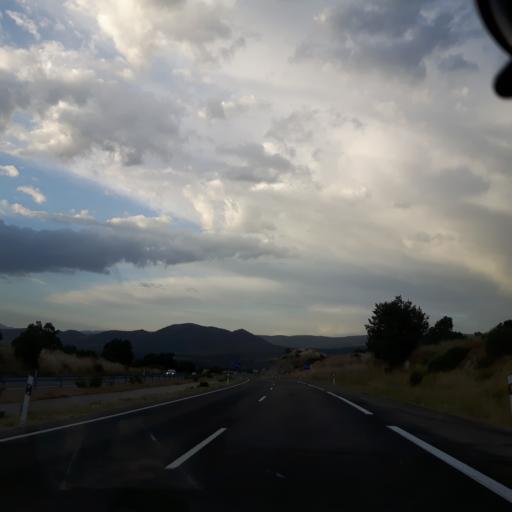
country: ES
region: Castille and Leon
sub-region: Provincia de Salamanca
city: Nava de Bejar
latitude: 40.4699
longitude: -5.6813
